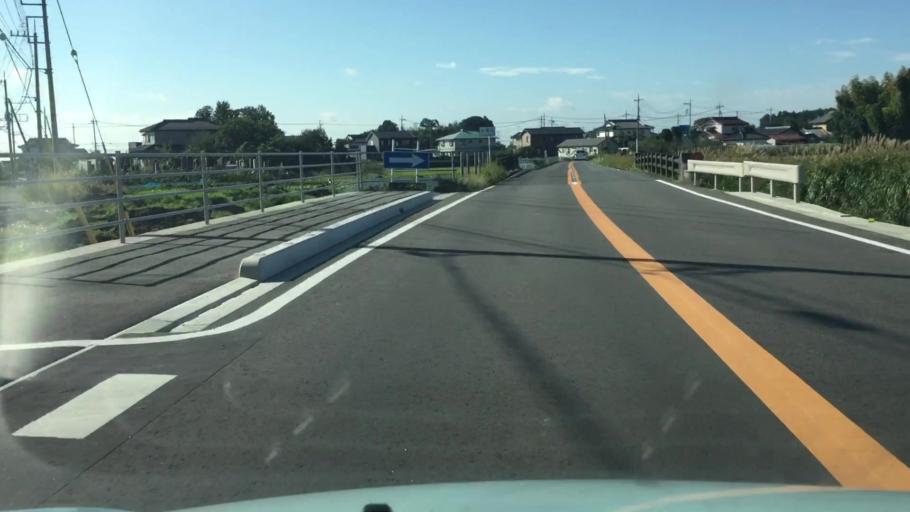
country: JP
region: Tochigi
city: Ujiie
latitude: 36.6510
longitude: 140.0210
